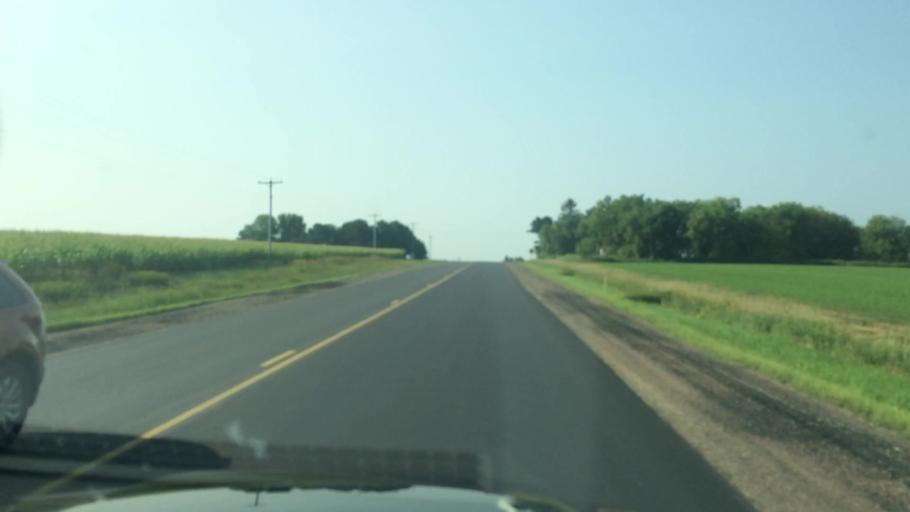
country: US
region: Wisconsin
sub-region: Marathon County
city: Stratford
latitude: 44.8911
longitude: -90.0789
